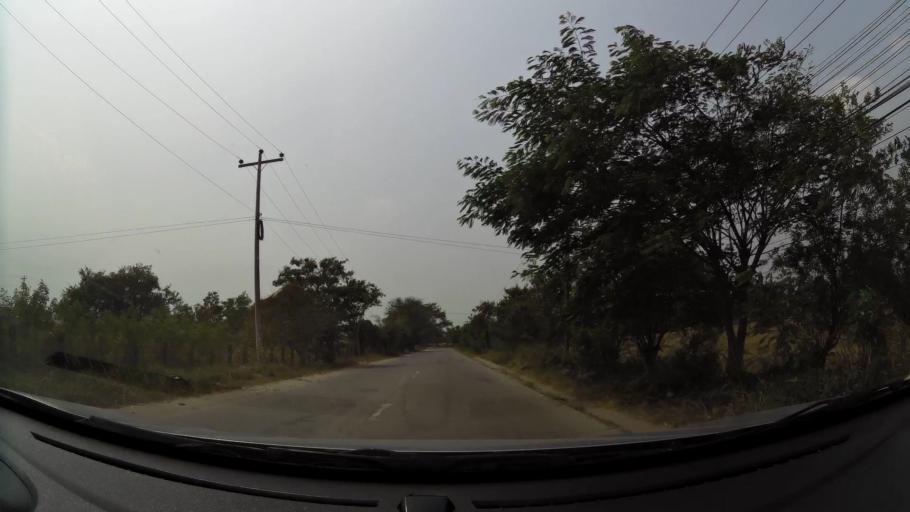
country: HN
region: Cortes
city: La Lima
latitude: 15.4346
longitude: -87.9037
